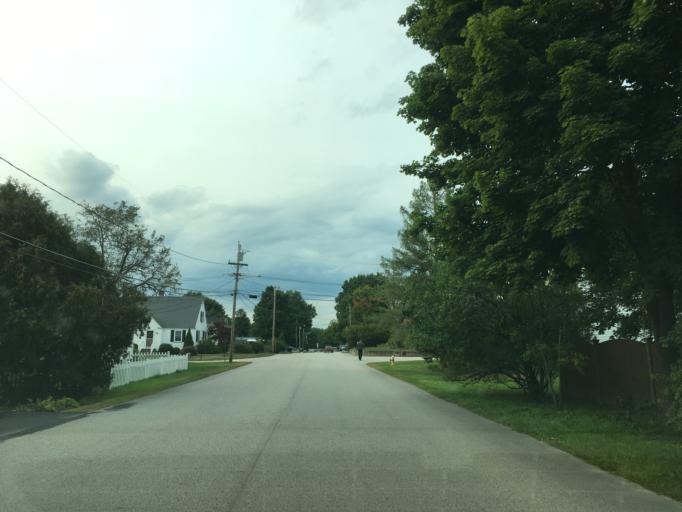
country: US
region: New Hampshire
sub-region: Rockingham County
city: Exeter
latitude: 42.9847
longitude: -70.9427
